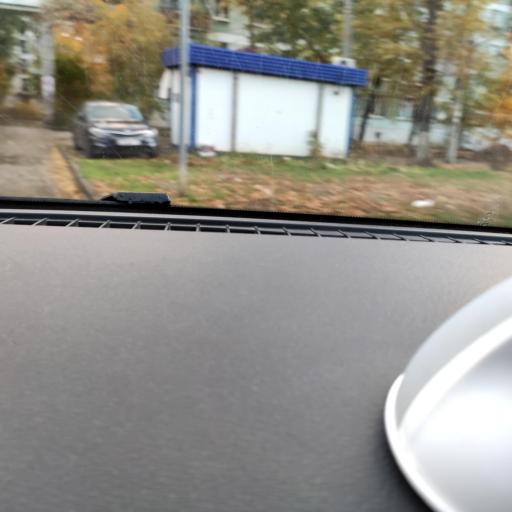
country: RU
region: Samara
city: Smyshlyayevka
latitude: 53.2288
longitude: 50.2964
